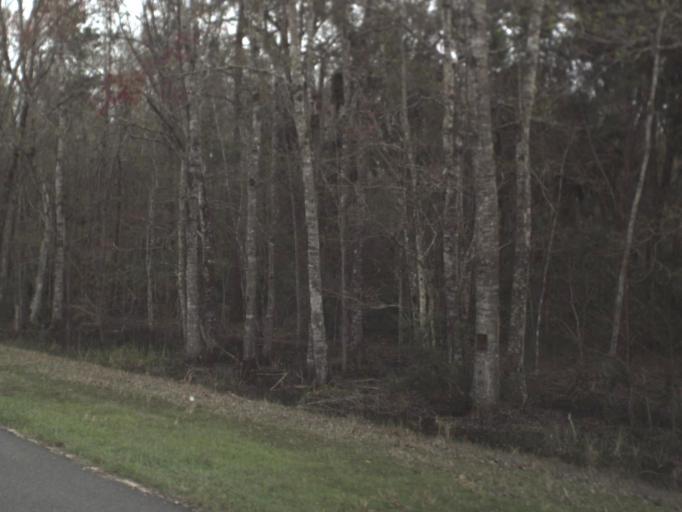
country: US
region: Florida
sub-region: Leon County
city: Woodville
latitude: 30.1585
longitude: -83.9992
